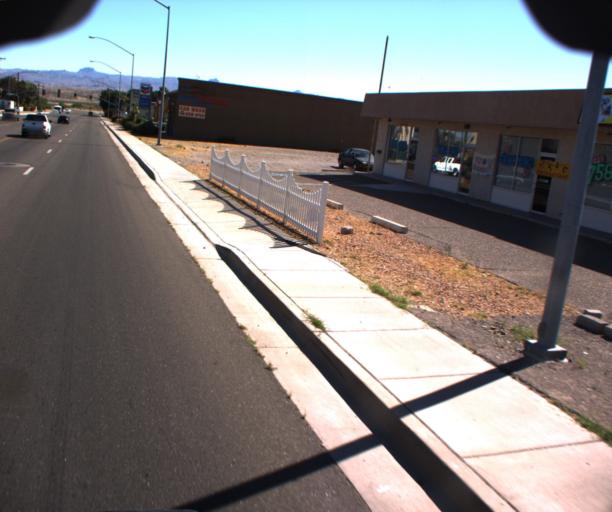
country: US
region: Arizona
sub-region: Mohave County
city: Bullhead City
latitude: 35.1257
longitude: -114.5784
